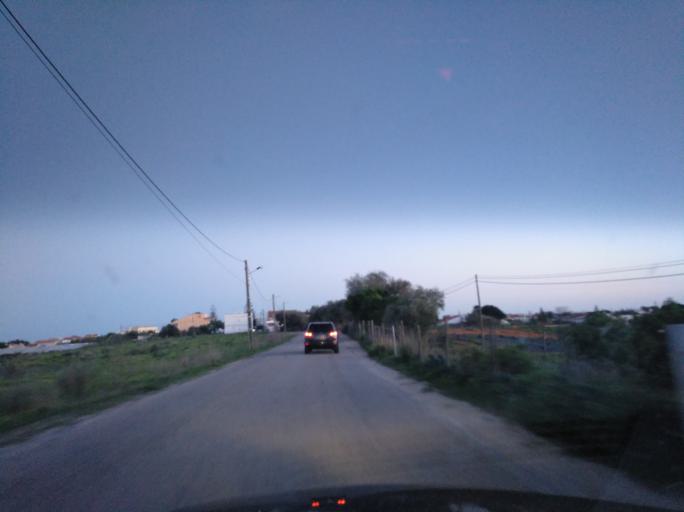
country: PT
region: Faro
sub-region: Vila Real de Santo Antonio
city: Monte Gordo
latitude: 37.1837
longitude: -7.5064
